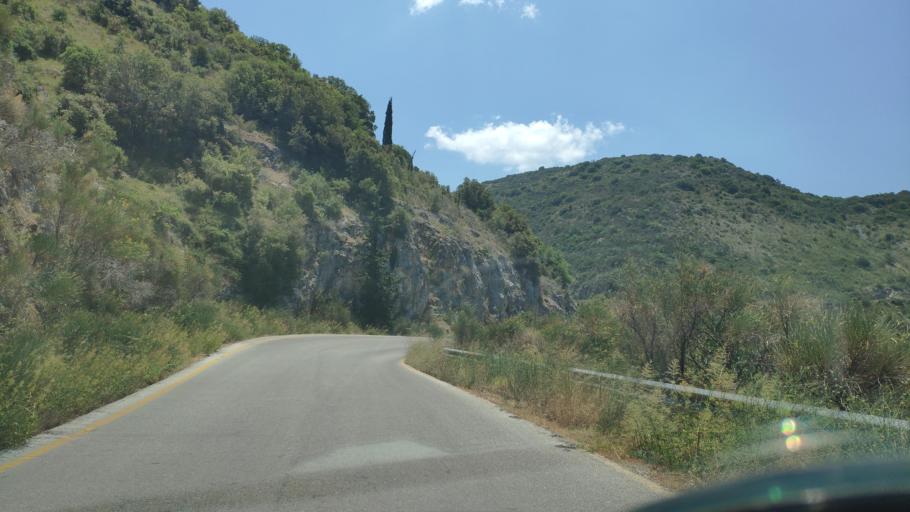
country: GR
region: Ionian Islands
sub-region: Lefkada
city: Nidri
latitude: 38.7480
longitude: 20.6204
